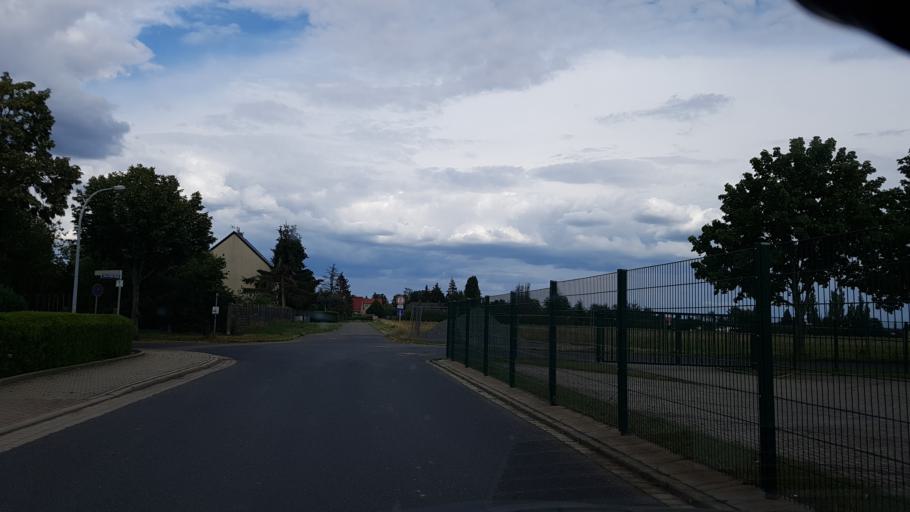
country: DE
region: Brandenburg
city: Falkenberg
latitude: 51.5786
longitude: 13.2342
